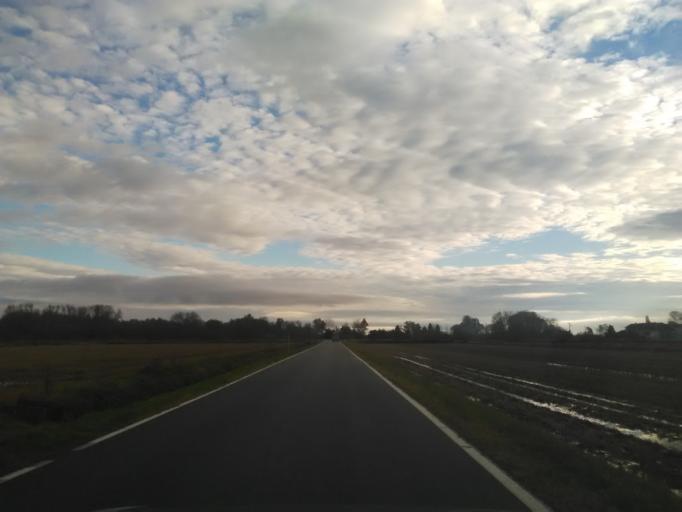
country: IT
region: Piedmont
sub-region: Provincia di Vercelli
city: Rovasenda
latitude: 45.5428
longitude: 8.3336
